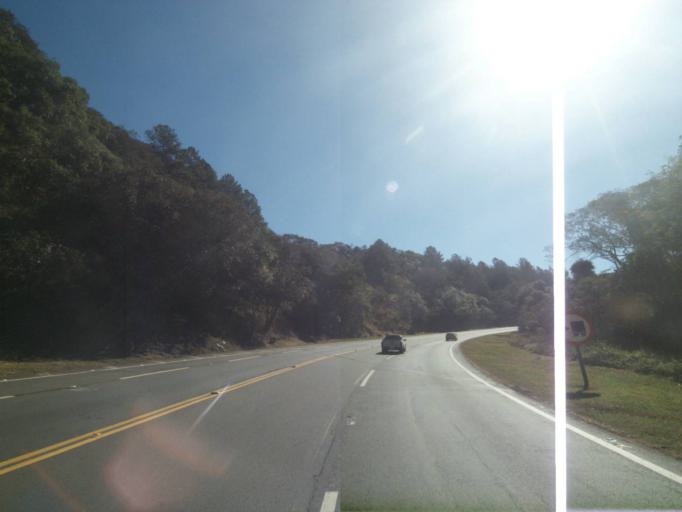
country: BR
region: Parana
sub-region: Tibagi
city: Tibagi
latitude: -24.7089
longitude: -50.5564
